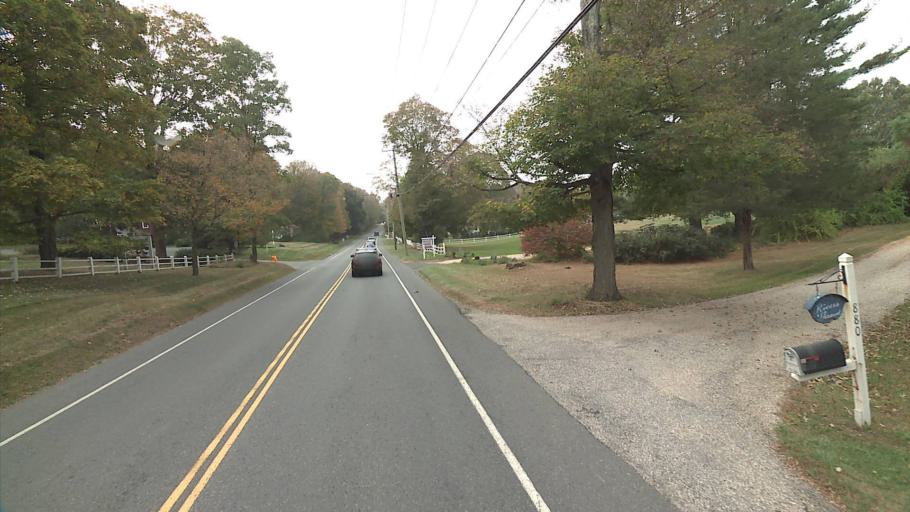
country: US
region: Connecticut
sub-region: Litchfield County
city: Woodbury Center
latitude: 41.5203
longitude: -73.2030
